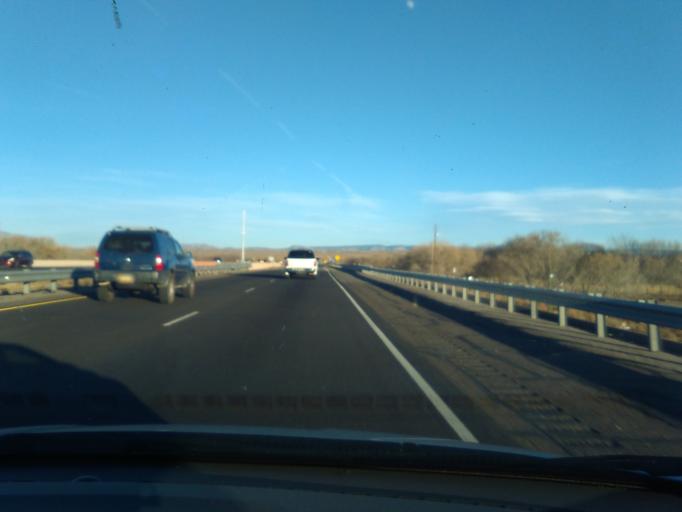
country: US
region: New Mexico
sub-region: Bernalillo County
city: South Valley
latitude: 34.9481
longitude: -106.6949
